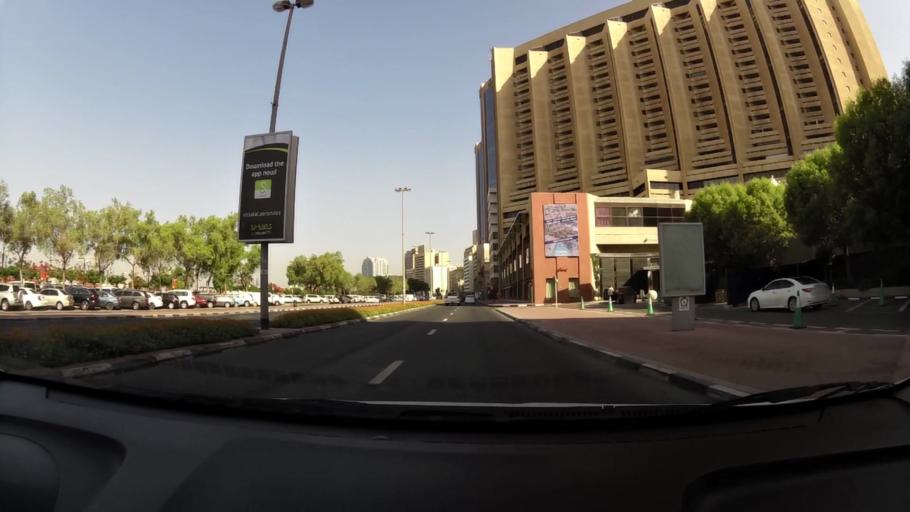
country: AE
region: Ash Shariqah
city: Sharjah
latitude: 25.2648
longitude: 55.3105
